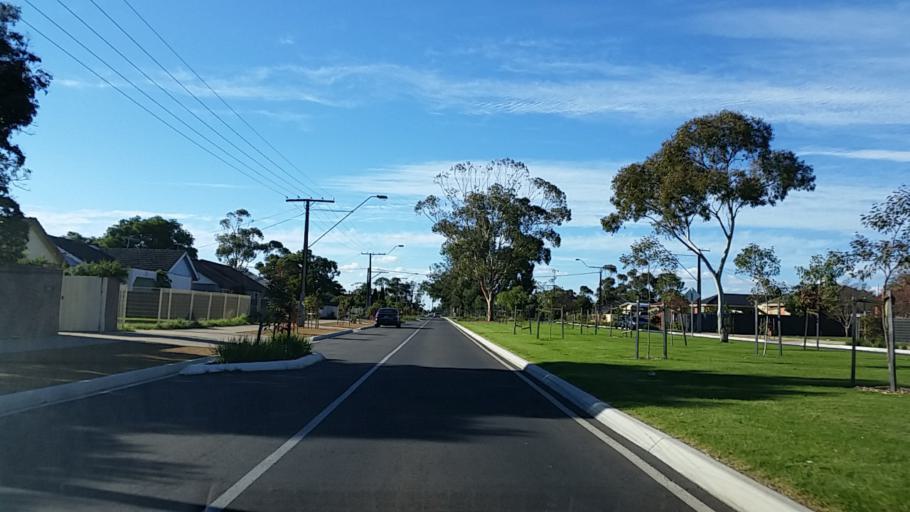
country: AU
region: South Australia
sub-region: Playford
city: Smithfield
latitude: -34.6839
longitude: 138.6713
